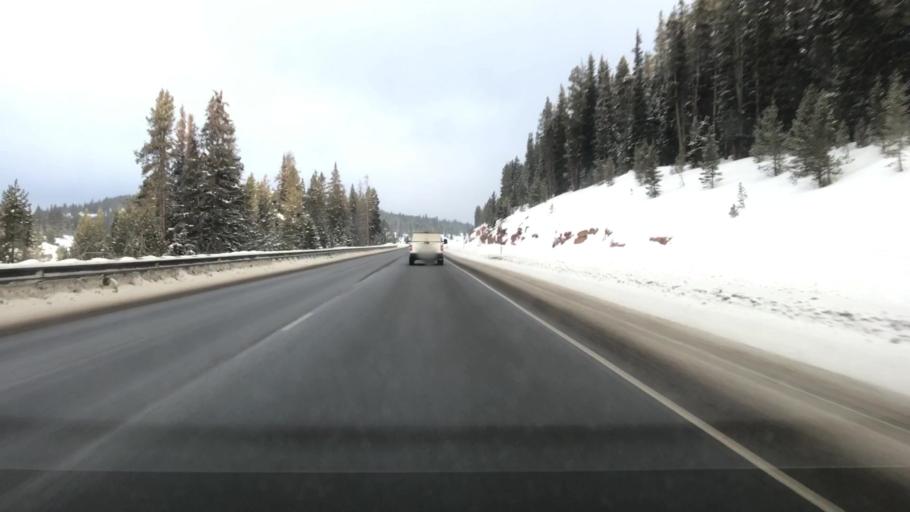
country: US
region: Colorado
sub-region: Summit County
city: Frisco
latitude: 39.5203
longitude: -106.2121
